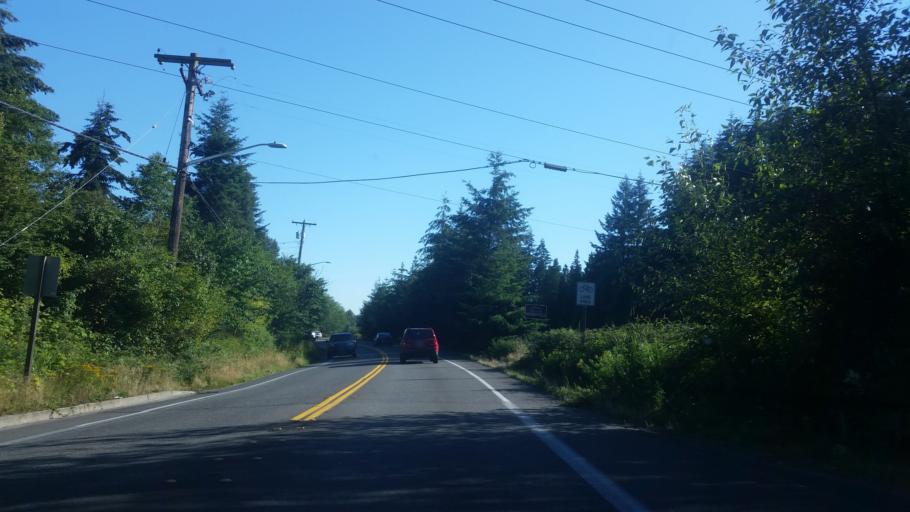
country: US
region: Washington
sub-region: King County
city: Woodinville
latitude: 47.7765
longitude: -122.1538
